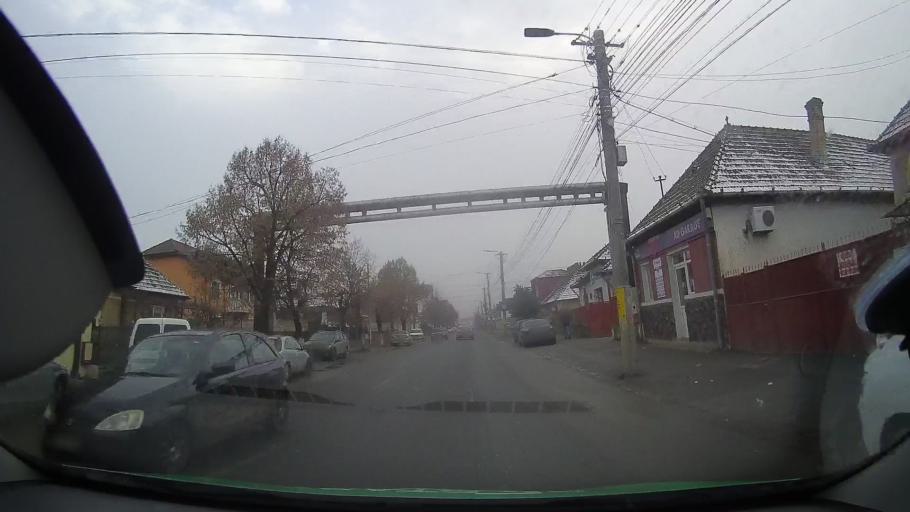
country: RO
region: Mures
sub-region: Municipiul Tarnaveni
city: Tarnaveni
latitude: 46.3202
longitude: 24.2963
